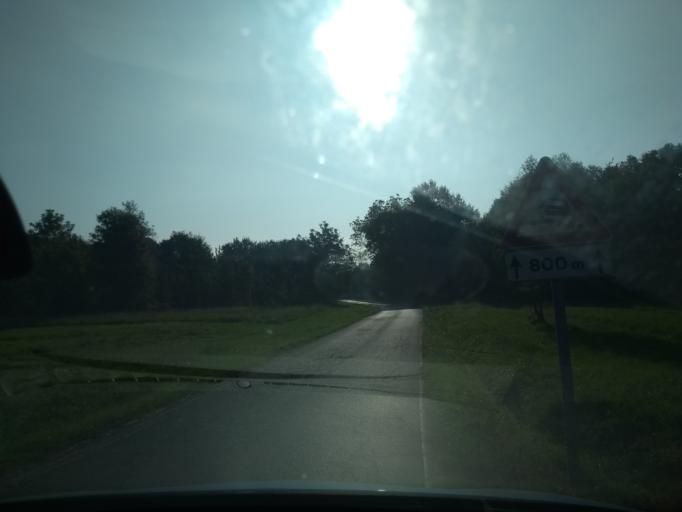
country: IT
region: Piedmont
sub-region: Provincia di Torino
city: Vallo Torinese
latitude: 45.2220
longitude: 7.5025
